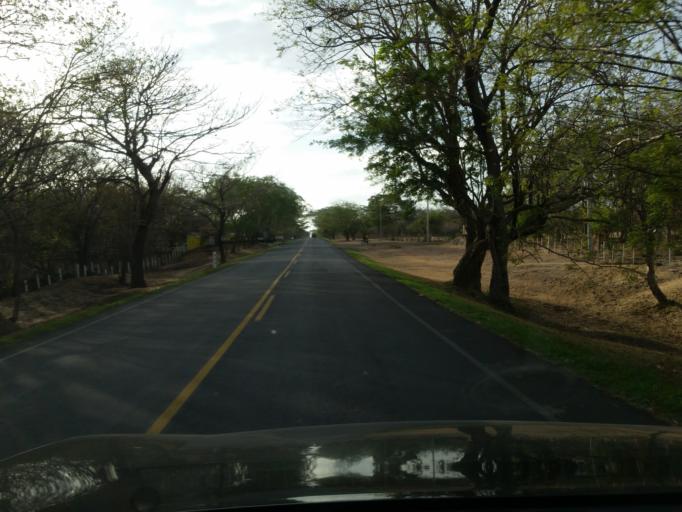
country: NI
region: Rivas
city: Belen
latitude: 11.5833
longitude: -85.9013
